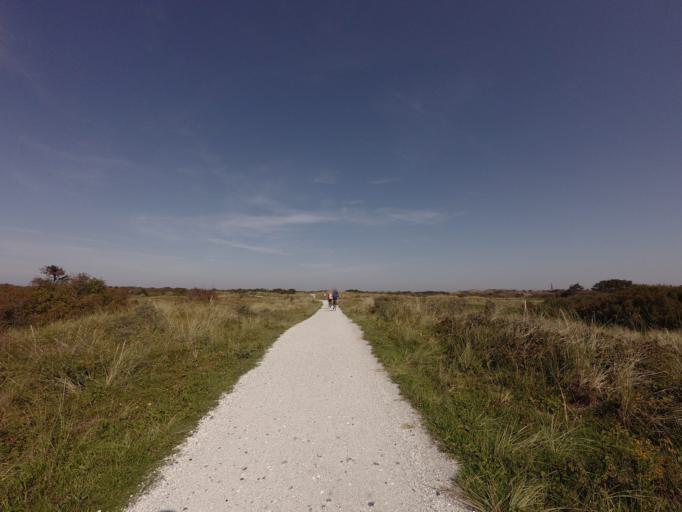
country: NL
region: Friesland
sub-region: Gemeente Schiermonnikoog
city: Schiermonnikoog
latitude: 53.4750
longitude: 6.1402
